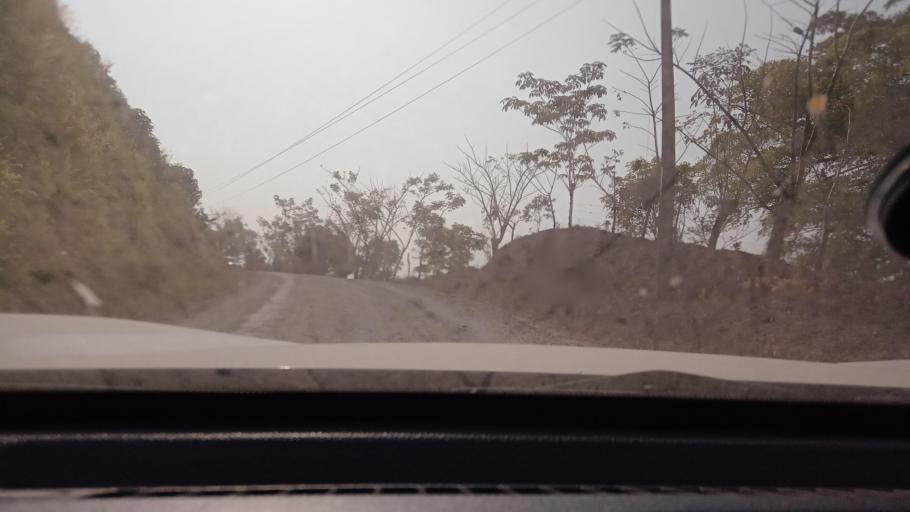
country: MX
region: Tabasco
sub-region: Huimanguillo
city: Francisco Rueda
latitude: 17.6206
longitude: -93.9429
